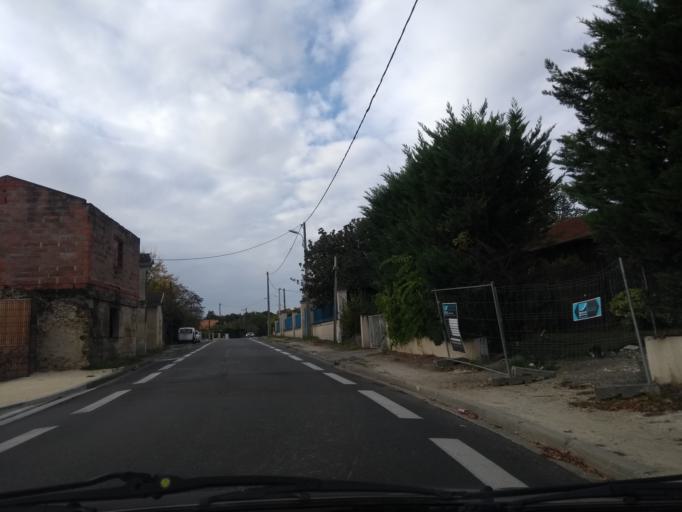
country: FR
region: Aquitaine
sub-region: Departement de la Gironde
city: Gradignan
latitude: 44.7740
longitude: -0.6245
